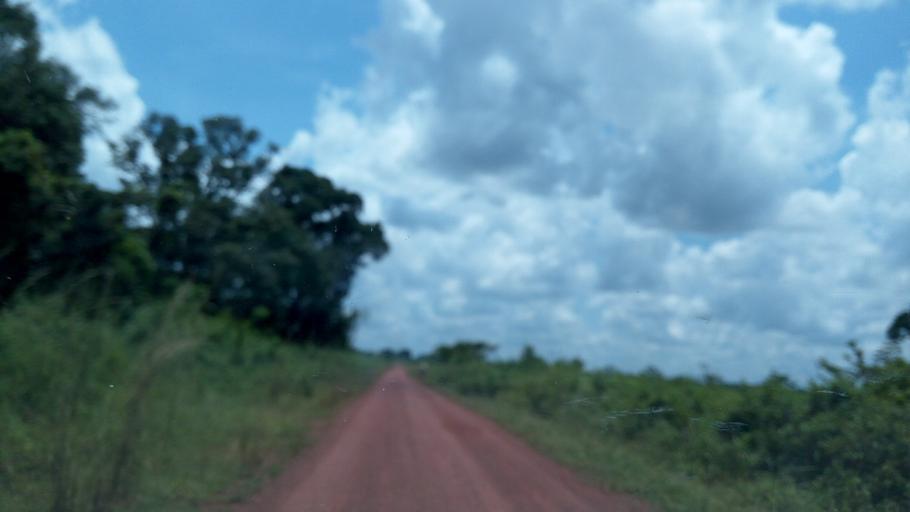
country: CD
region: Equateur
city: Libenge
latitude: 3.7735
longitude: 18.9383
